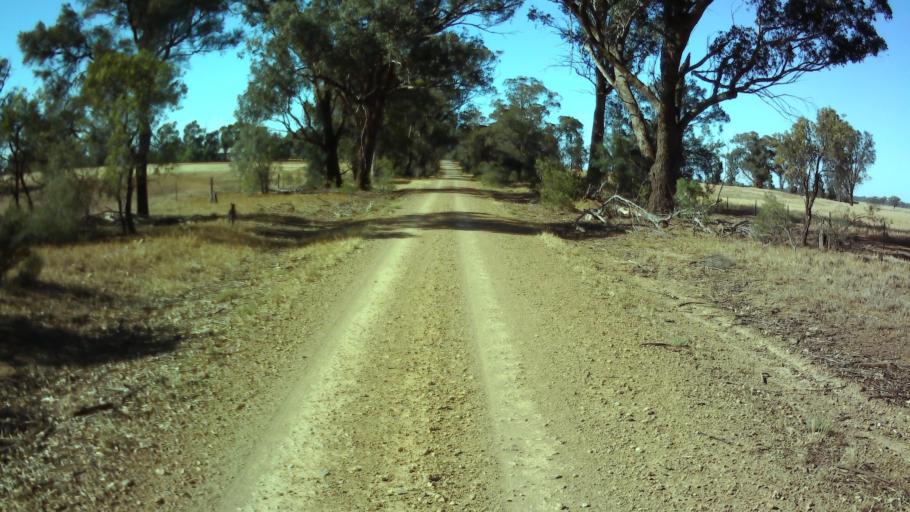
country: AU
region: New South Wales
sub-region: Weddin
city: Grenfell
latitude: -33.9227
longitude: 147.8745
